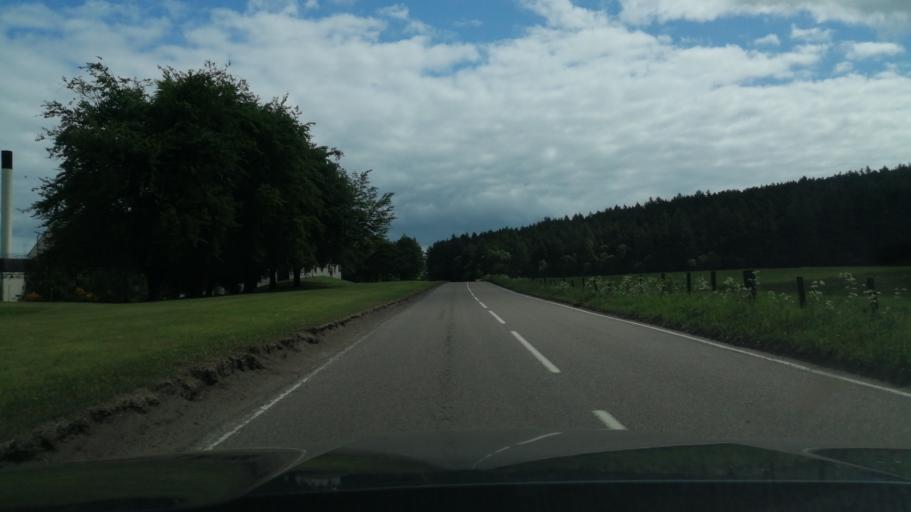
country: GB
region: Scotland
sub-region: Moray
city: Fochabers
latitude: 57.5468
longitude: -3.1162
